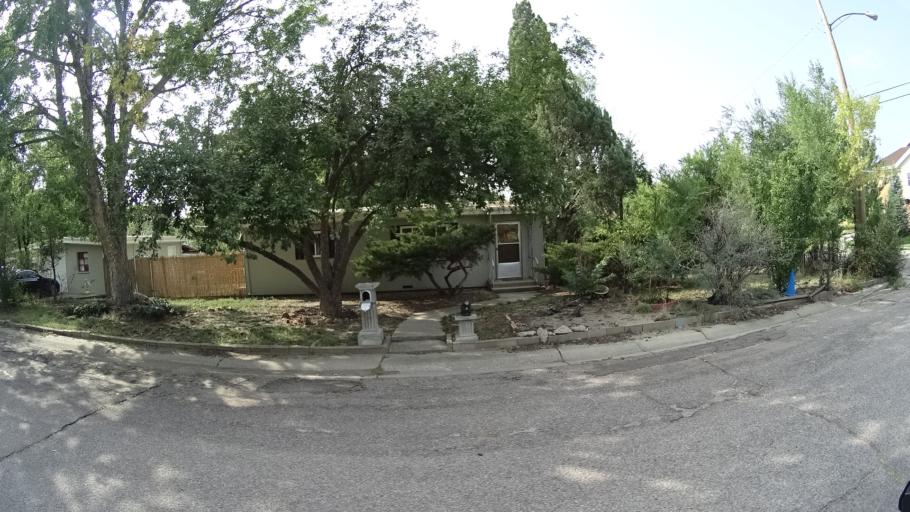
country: US
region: Colorado
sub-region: El Paso County
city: Colorado Springs
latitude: 38.8449
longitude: -104.7823
